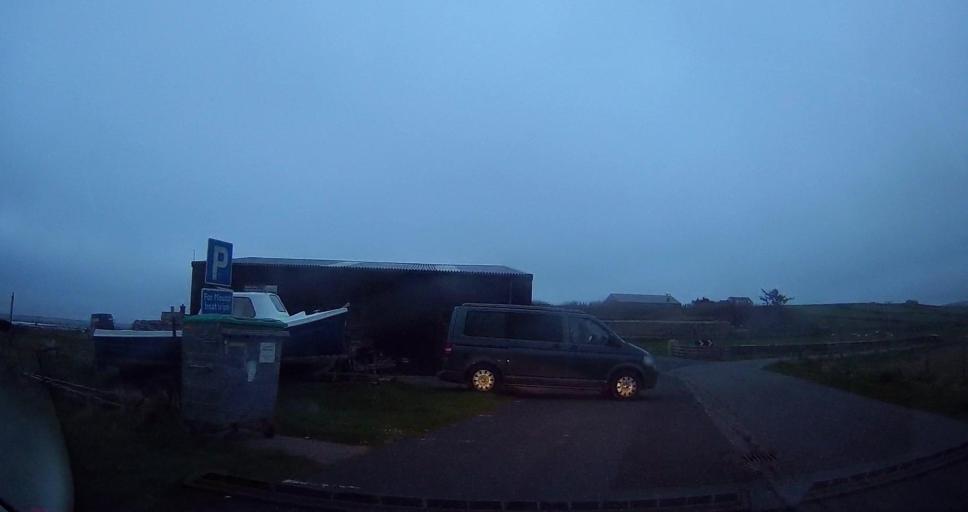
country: GB
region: Scotland
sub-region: Shetland Islands
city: Sandwick
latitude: 60.0064
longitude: -1.2214
